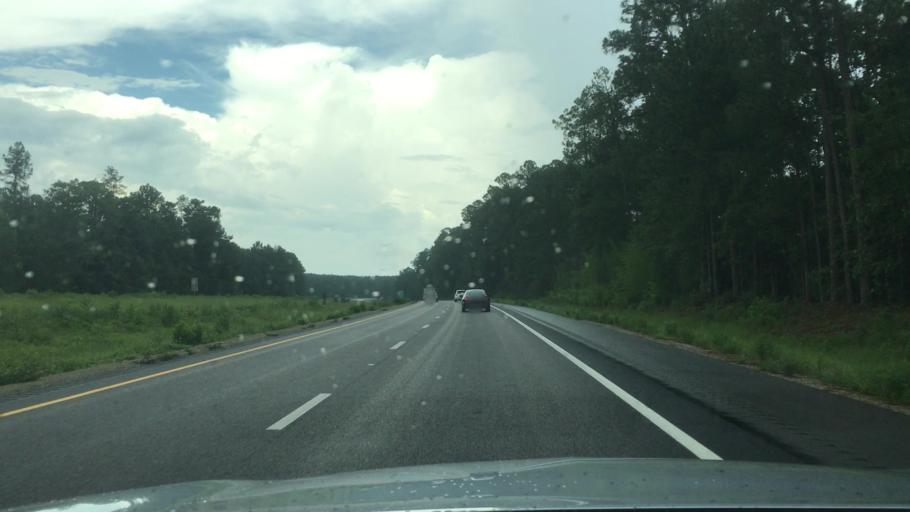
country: US
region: Mississippi
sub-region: Forrest County
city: Hattiesburg
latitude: 31.2293
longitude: -89.3227
